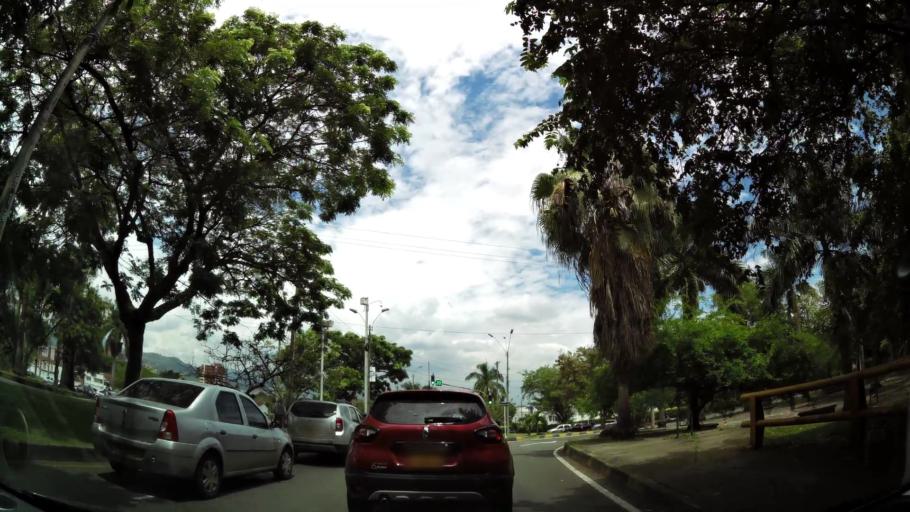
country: CO
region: Valle del Cauca
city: Cali
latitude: 3.3873
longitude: -76.5325
